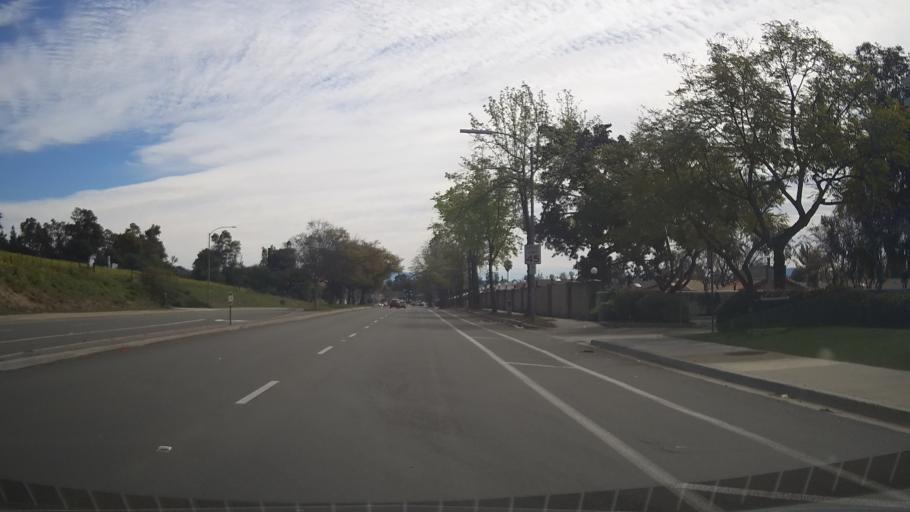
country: US
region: California
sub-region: San Diego County
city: Escondido
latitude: 33.1454
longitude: -117.1011
